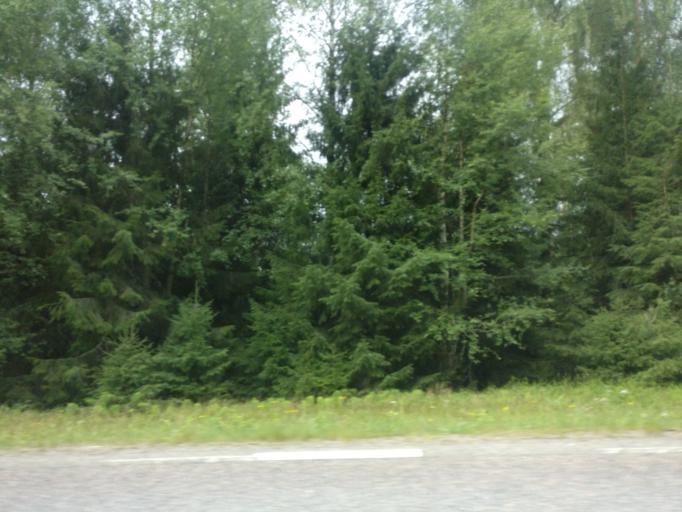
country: SE
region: Vaermland
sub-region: Torsby Kommun
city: Torsby
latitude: 60.7728
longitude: 12.7521
